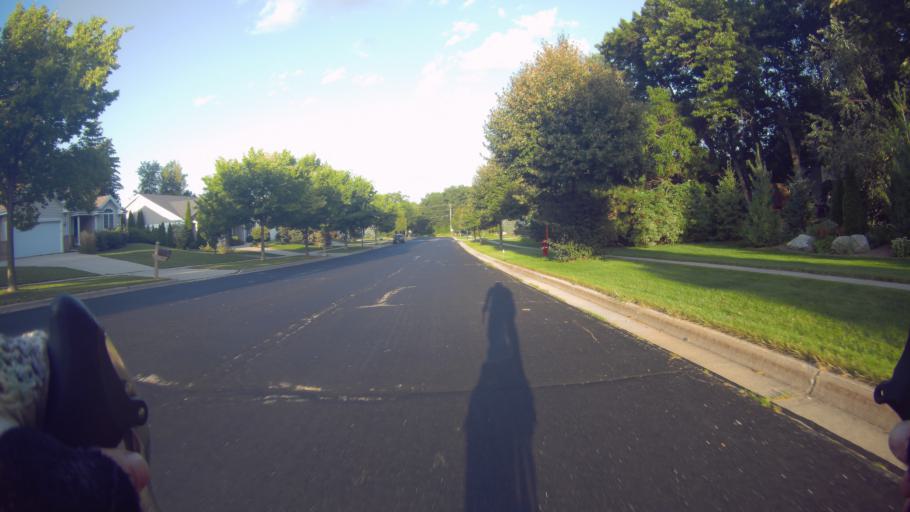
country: US
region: Wisconsin
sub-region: Dane County
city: Madison
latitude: 43.0222
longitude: -89.4278
